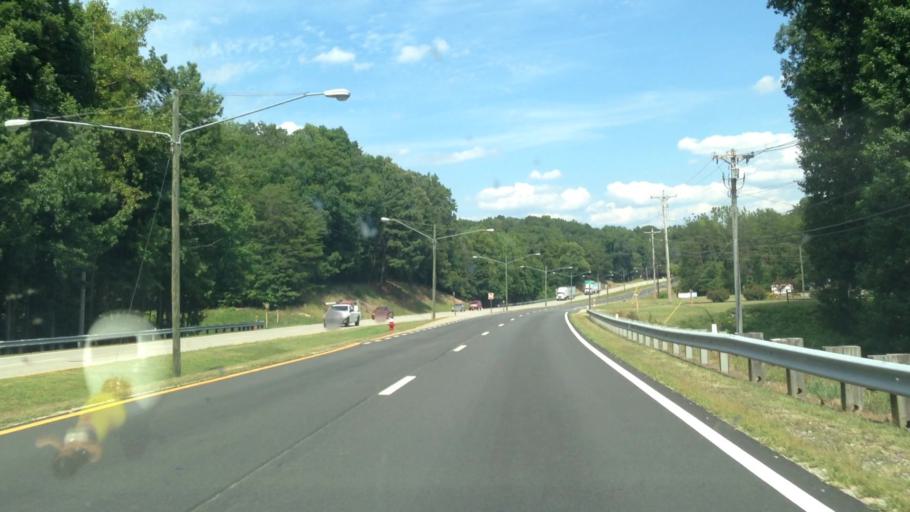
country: US
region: Virginia
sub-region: City of Danville
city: Danville
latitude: 36.5976
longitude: -79.4840
